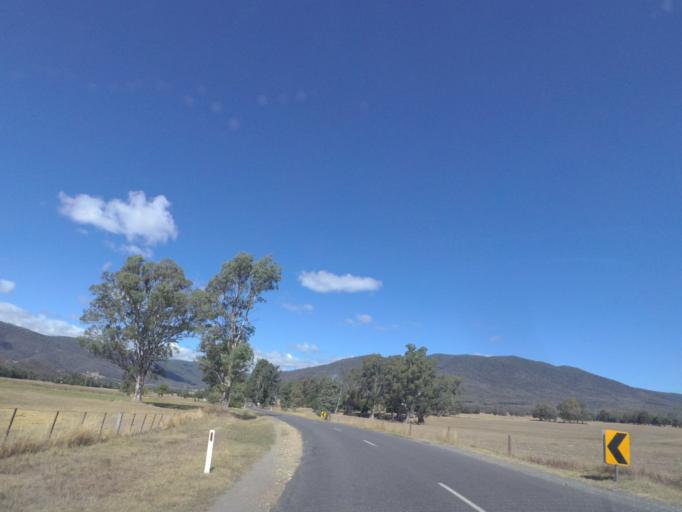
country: AU
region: Victoria
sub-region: Murrindindi
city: Alexandra
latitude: -37.2860
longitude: 145.8040
